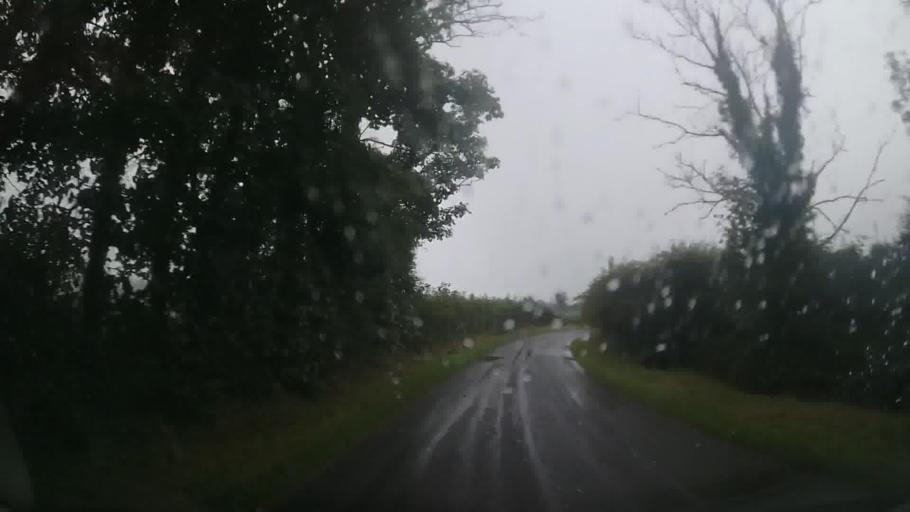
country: GB
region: Wales
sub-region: Carmarthenshire
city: Whitland
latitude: 51.7613
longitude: -4.6361
